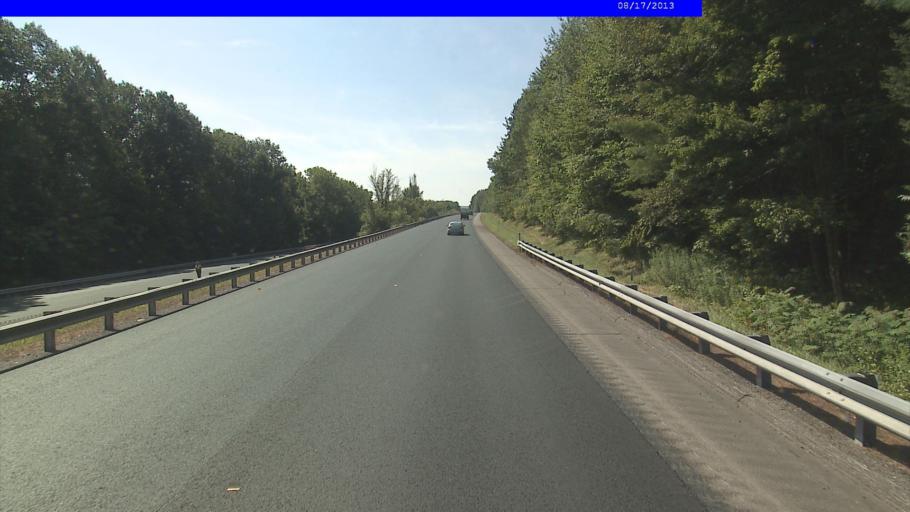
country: US
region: New Hampshire
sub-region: Cheshire County
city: Chesterfield
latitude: 42.9341
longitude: -72.5279
